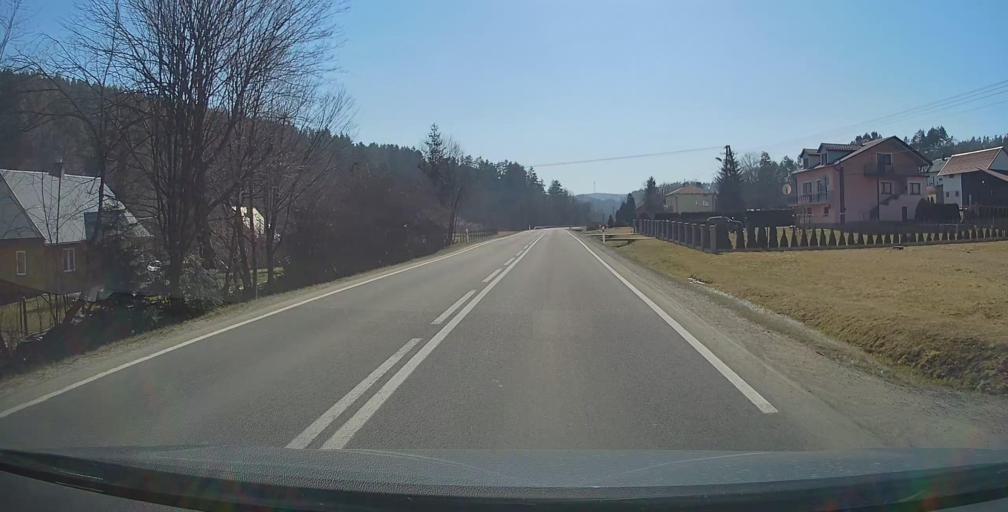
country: PL
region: Subcarpathian Voivodeship
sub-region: Powiat przemyski
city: Bircza
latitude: 49.6805
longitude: 22.4371
